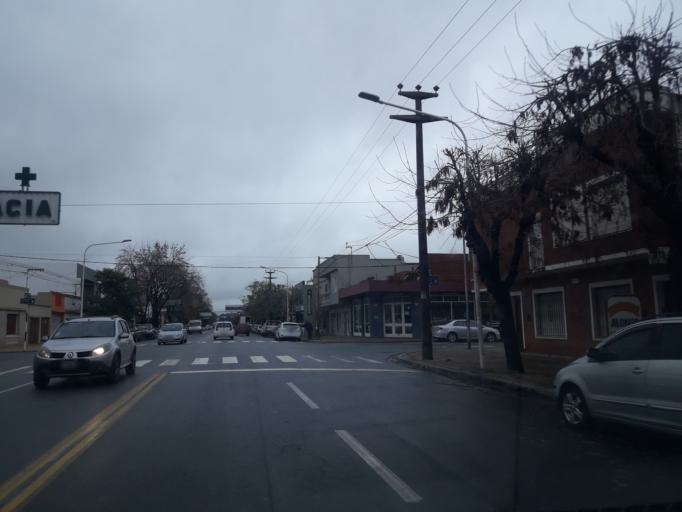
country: AR
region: Buenos Aires
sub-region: Partido de Tandil
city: Tandil
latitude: -37.3226
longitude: -59.1491
